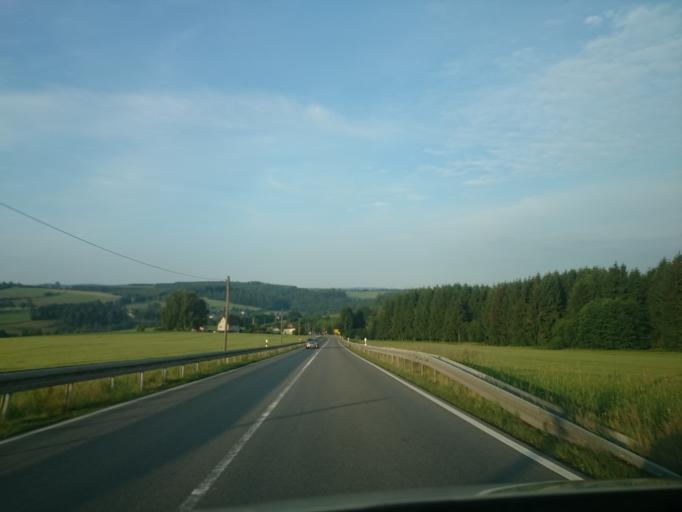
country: DE
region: Saxony
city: Pockau
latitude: 50.7345
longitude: 13.2734
